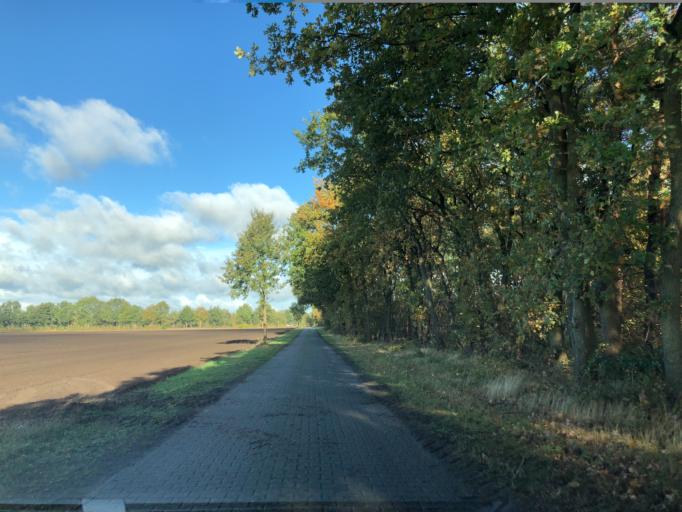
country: DE
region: Lower Saxony
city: Neulehe
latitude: 53.0237
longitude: 7.3673
